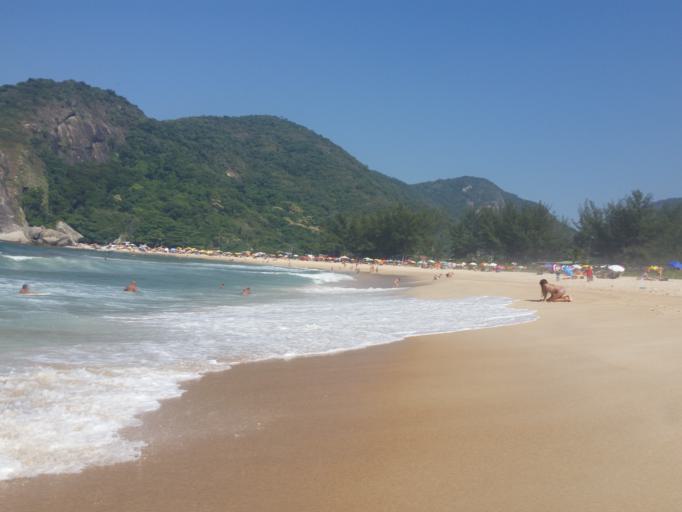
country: BR
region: Rio de Janeiro
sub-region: Nilopolis
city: Nilopolis
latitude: -23.0502
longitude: -43.5335
